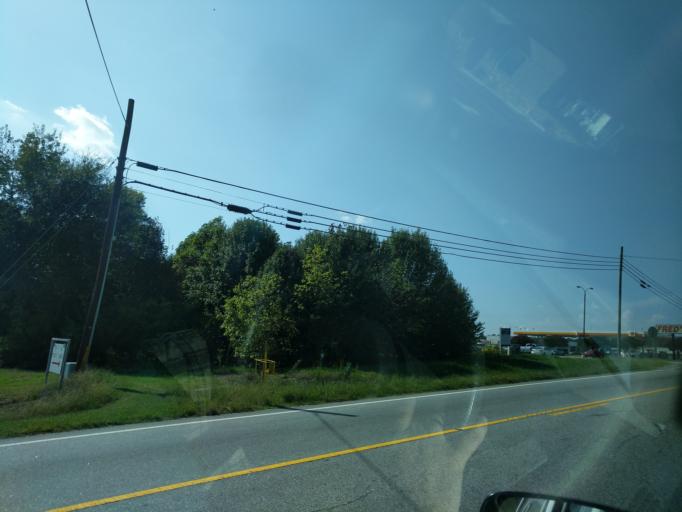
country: US
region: Georgia
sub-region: Franklin County
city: Lavonia
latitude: 34.4219
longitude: -83.1024
